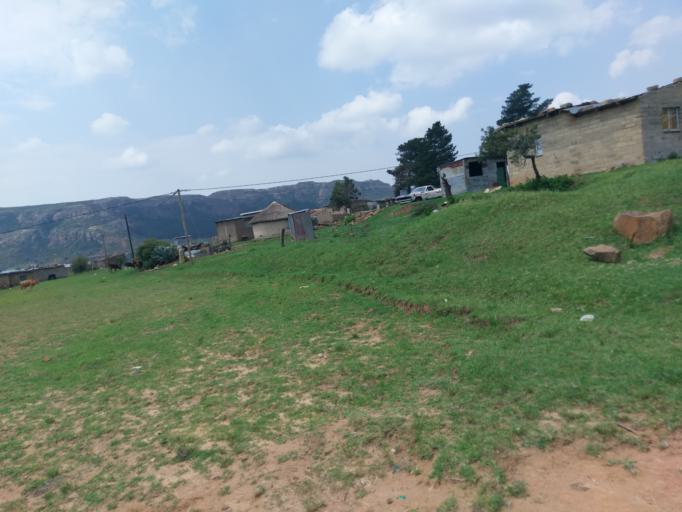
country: LS
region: Leribe
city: Leribe
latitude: -29.0231
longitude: 28.0161
